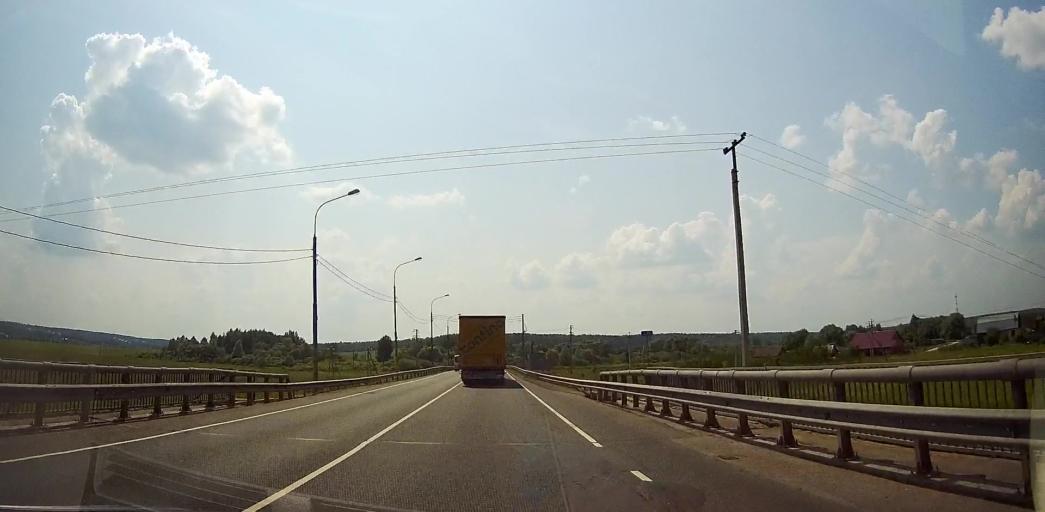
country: RU
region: Moskovskaya
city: Meshcherino
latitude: 55.1897
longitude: 38.3603
